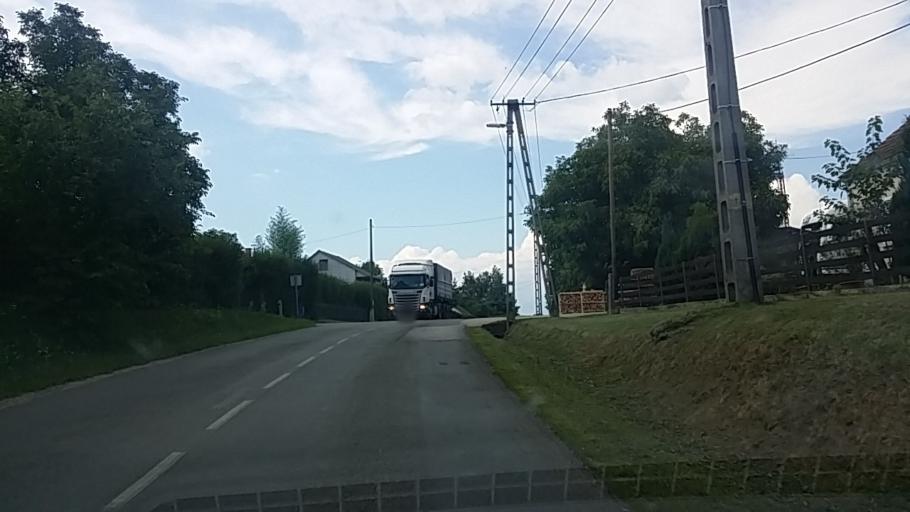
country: HU
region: Zala
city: Becsehely
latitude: 46.5142
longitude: 16.7781
